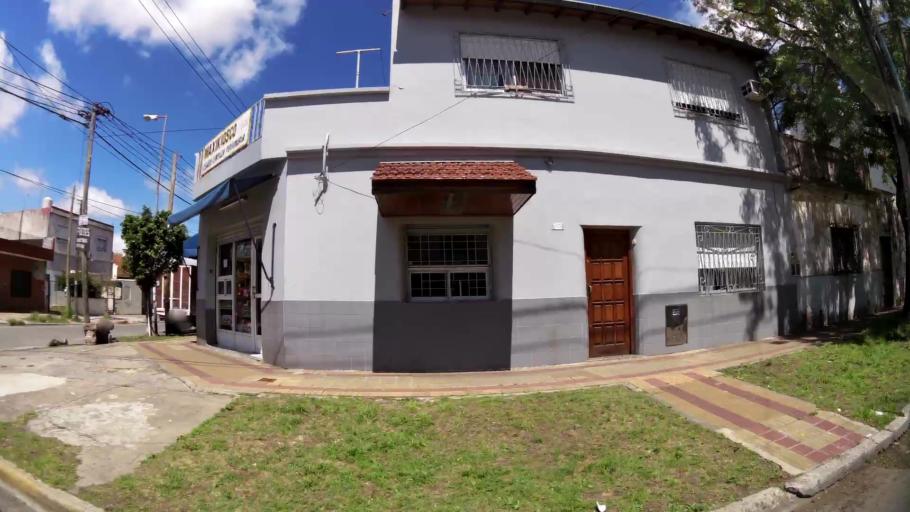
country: AR
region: Buenos Aires
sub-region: Partido de Lanus
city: Lanus
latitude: -34.6906
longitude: -58.4317
